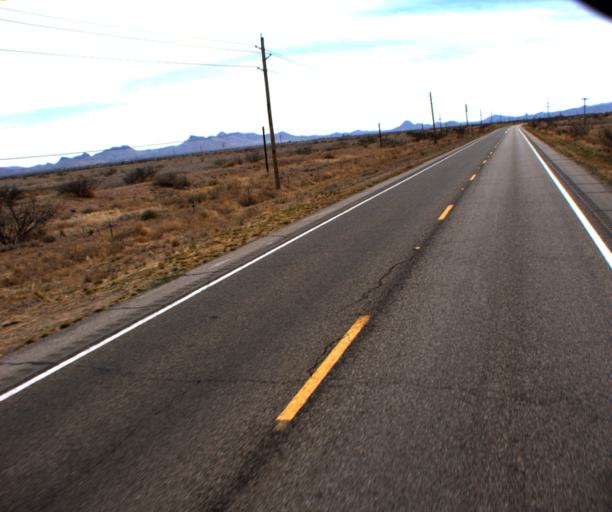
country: US
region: Arizona
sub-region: Cochise County
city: Pirtleville
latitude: 31.4389
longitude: -109.5934
